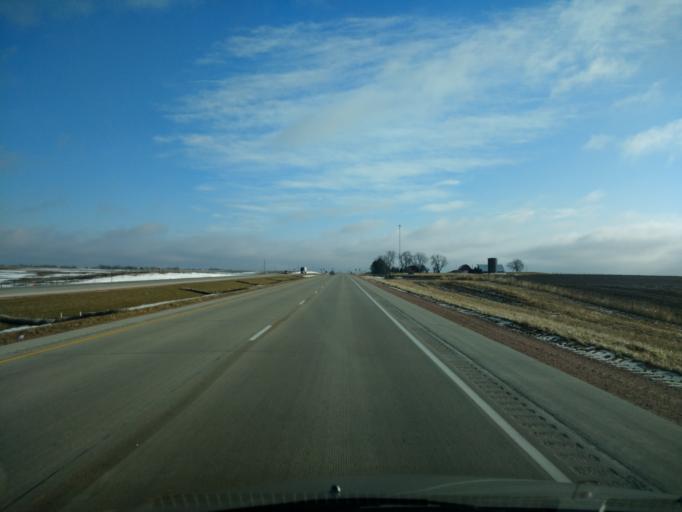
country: US
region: Iowa
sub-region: Ida County
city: Holstein
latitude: 42.4746
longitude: -95.5592
